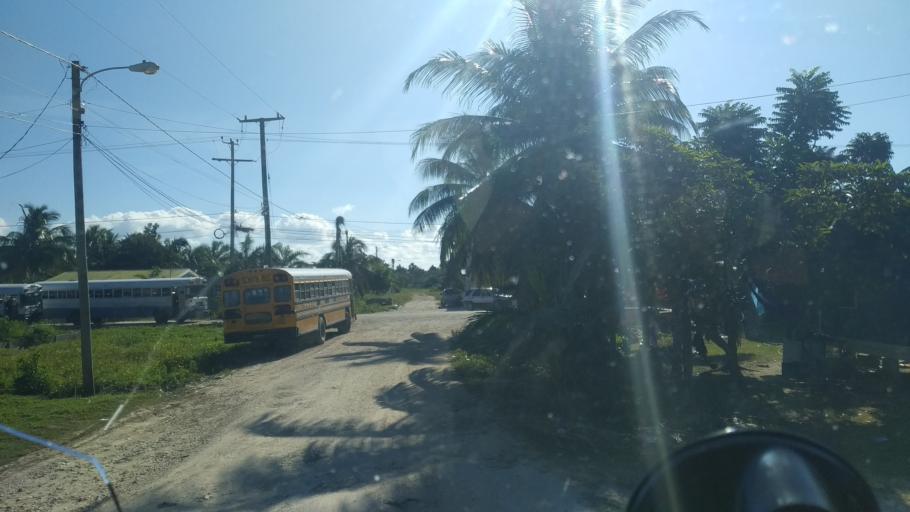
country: BZ
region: Belize
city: Belize City
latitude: 17.5506
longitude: -88.3247
